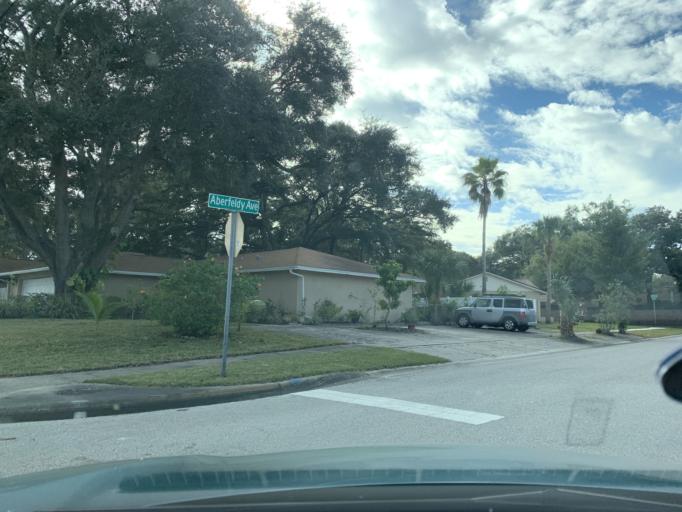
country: US
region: Florida
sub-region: Pinellas County
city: Kenneth City
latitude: 27.8247
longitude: -82.7369
